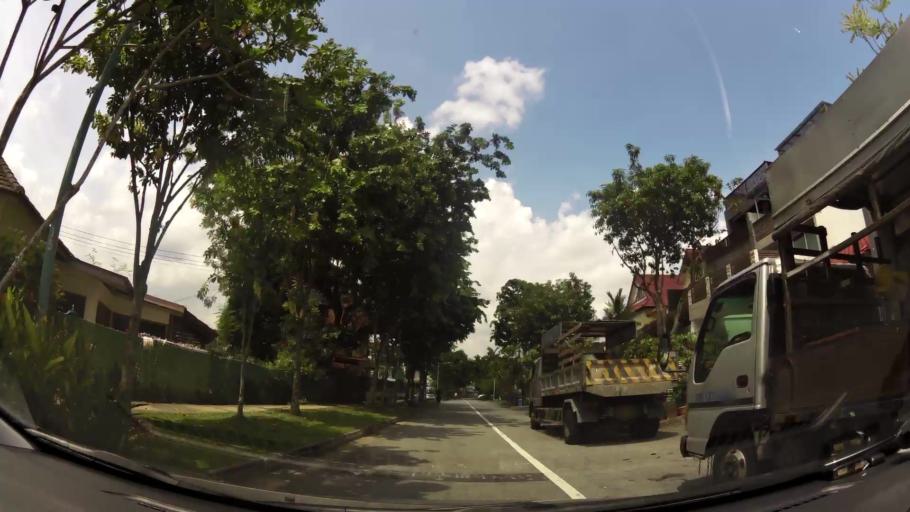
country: SG
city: Singapore
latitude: 1.3756
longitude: 103.8308
